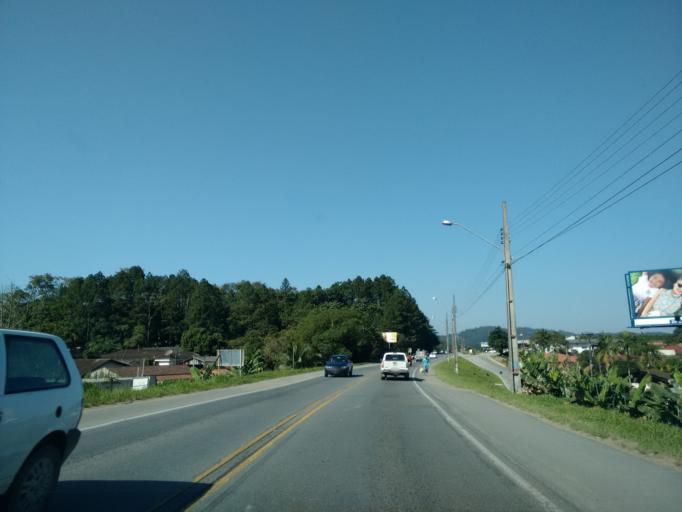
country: BR
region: Santa Catarina
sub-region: Guaramirim
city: Guaramirim
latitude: -26.4746
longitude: -49.0188
